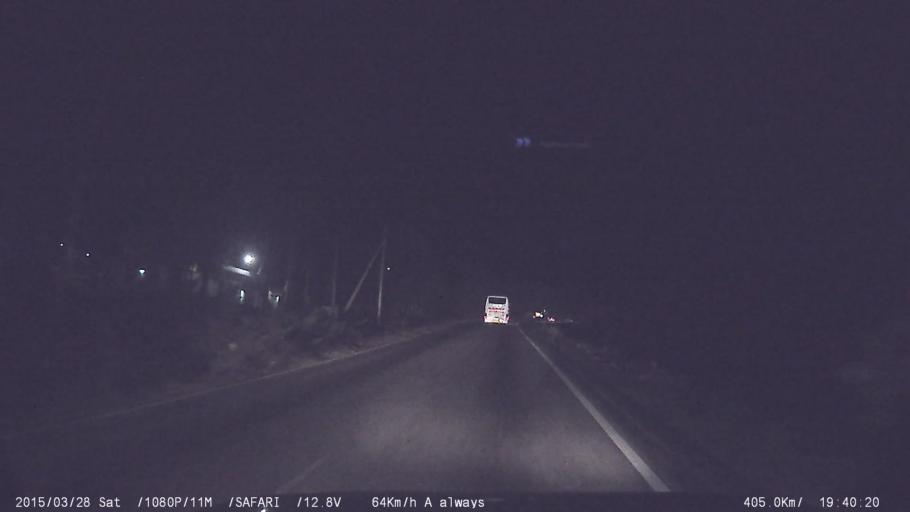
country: IN
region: Karnataka
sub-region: Mandya
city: Shrirangapattana
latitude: 12.4517
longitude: 76.7386
